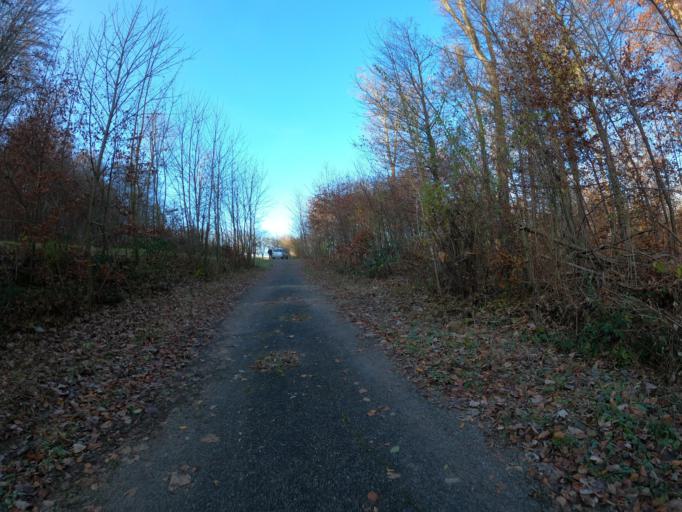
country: DE
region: Baden-Wuerttemberg
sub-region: Regierungsbezirk Stuttgart
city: Albershausen
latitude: 48.7055
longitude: 9.5693
